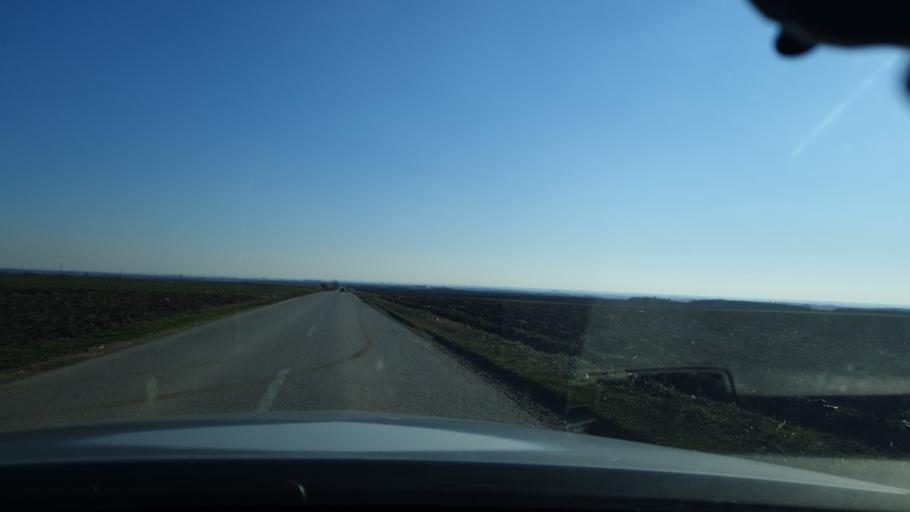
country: RS
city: Vrdnik
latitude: 45.0861
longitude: 19.8068
